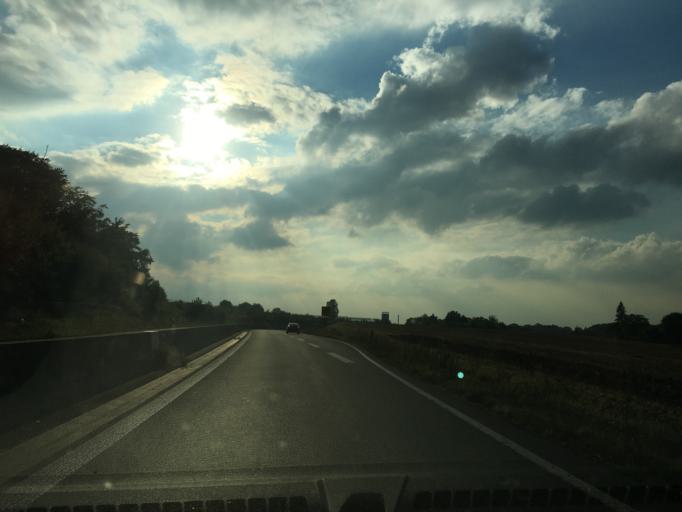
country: DE
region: North Rhine-Westphalia
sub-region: Regierungsbezirk Munster
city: Dulmen
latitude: 51.8456
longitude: 7.3034
